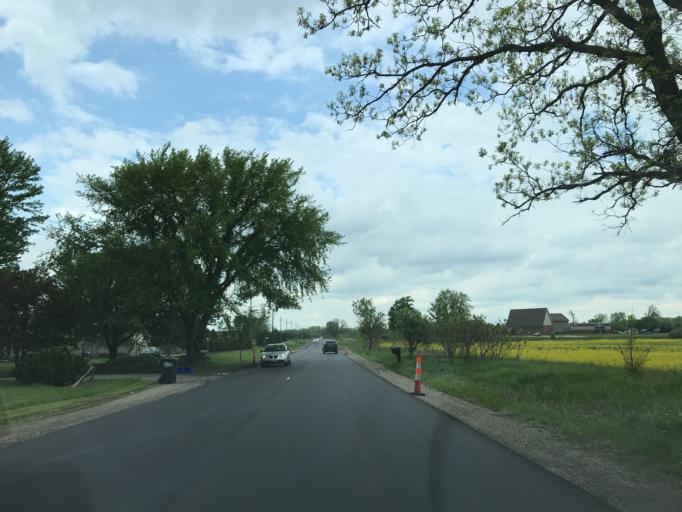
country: US
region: Michigan
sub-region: Oakland County
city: South Lyon
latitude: 42.4966
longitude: -83.6537
